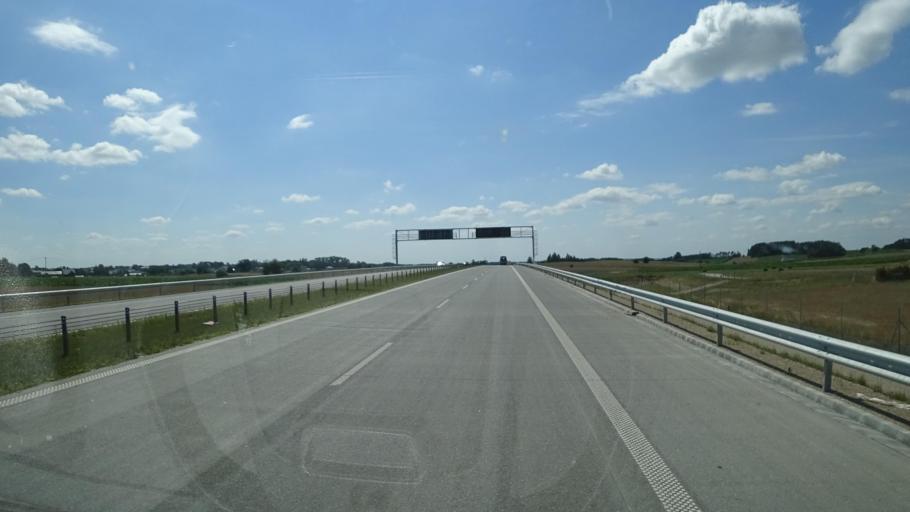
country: PL
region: Podlasie
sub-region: Powiat lomzynski
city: Piatnica
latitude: 53.2627
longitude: 22.1183
